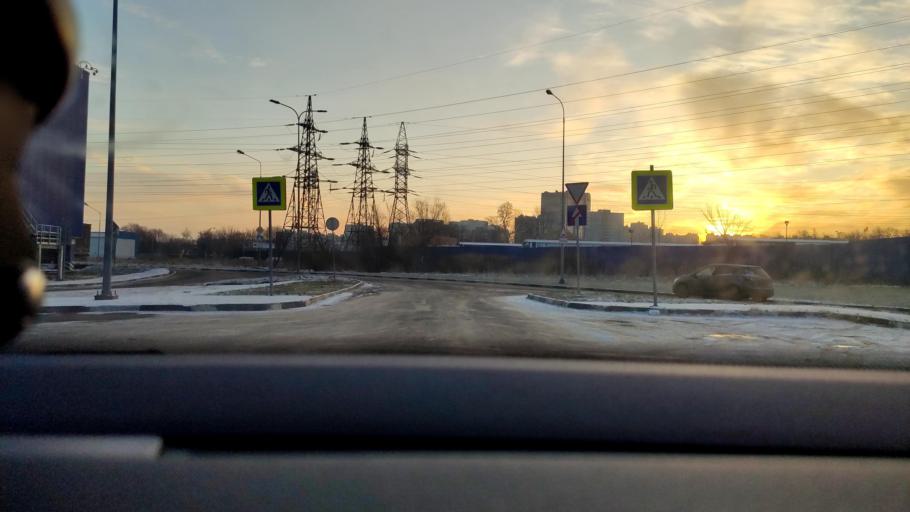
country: RU
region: Moskovskaya
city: Kotel'niki
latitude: 55.6520
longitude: 37.8467
